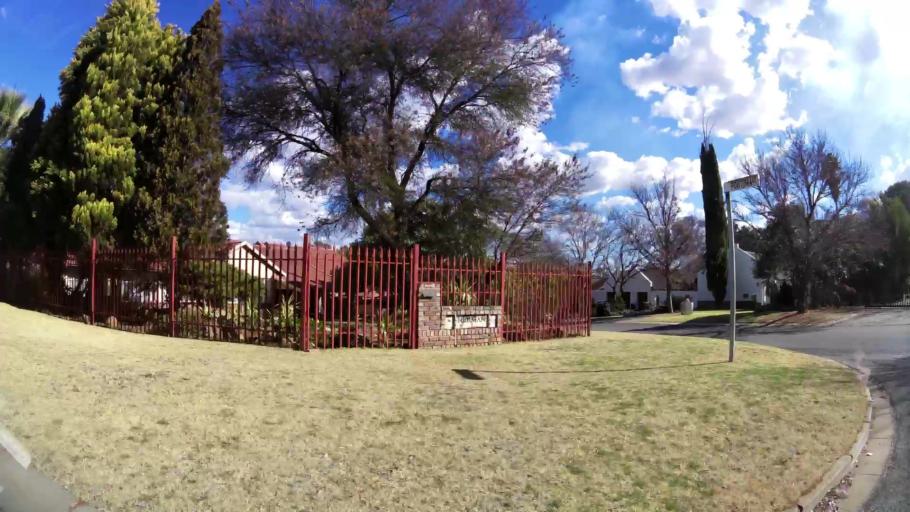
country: ZA
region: North-West
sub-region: Dr Kenneth Kaunda District Municipality
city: Klerksdorp
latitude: -26.8448
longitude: 26.6446
